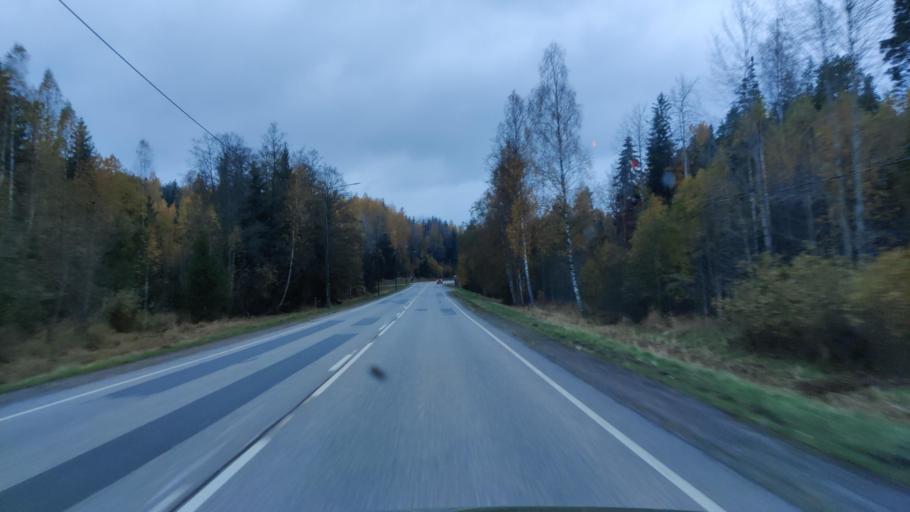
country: FI
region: Uusimaa
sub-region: Helsinki
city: Vihti
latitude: 60.3238
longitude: 24.2178
